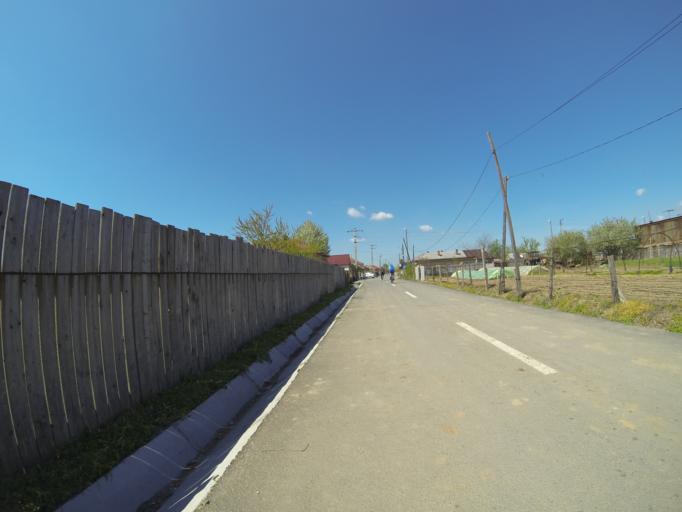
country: RO
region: Dolj
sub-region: Comuna Isalnita
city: Isalnita
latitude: 44.3912
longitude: 23.7482
